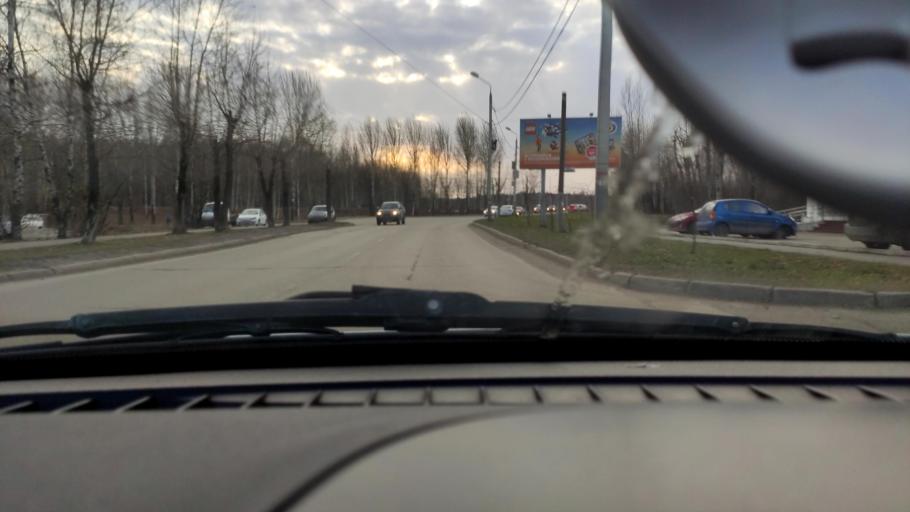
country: RU
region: Perm
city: Perm
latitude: 58.1028
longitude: 56.3880
